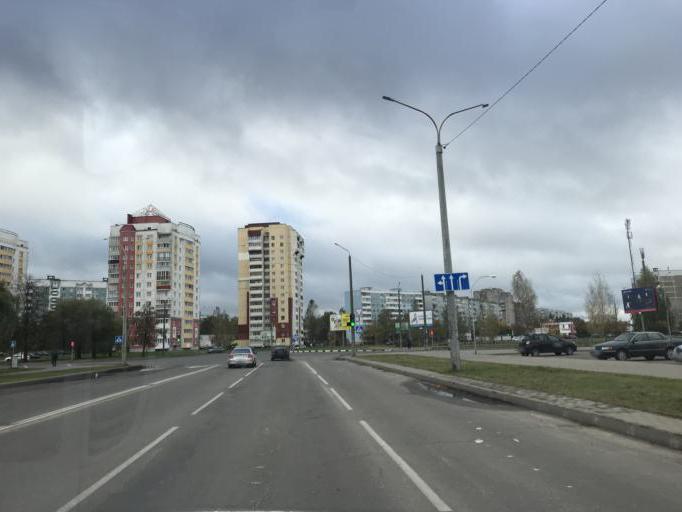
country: BY
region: Mogilev
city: Mahilyow
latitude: 53.8806
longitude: 30.3688
